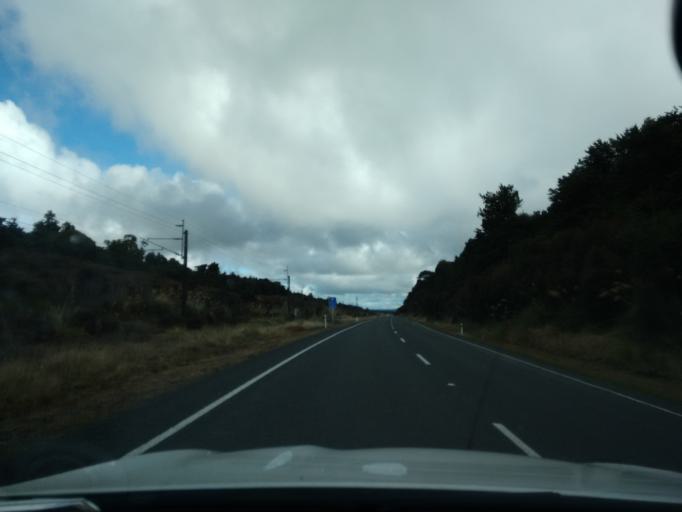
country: NZ
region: Manawatu-Wanganui
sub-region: Ruapehu District
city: Waiouru
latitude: -39.3085
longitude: 175.3896
